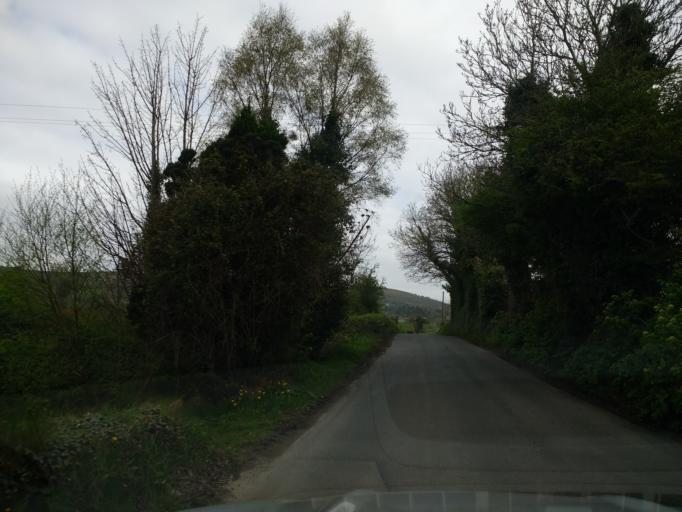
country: IE
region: Ulster
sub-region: County Donegal
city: Buncrana
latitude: 55.1012
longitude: -7.5348
